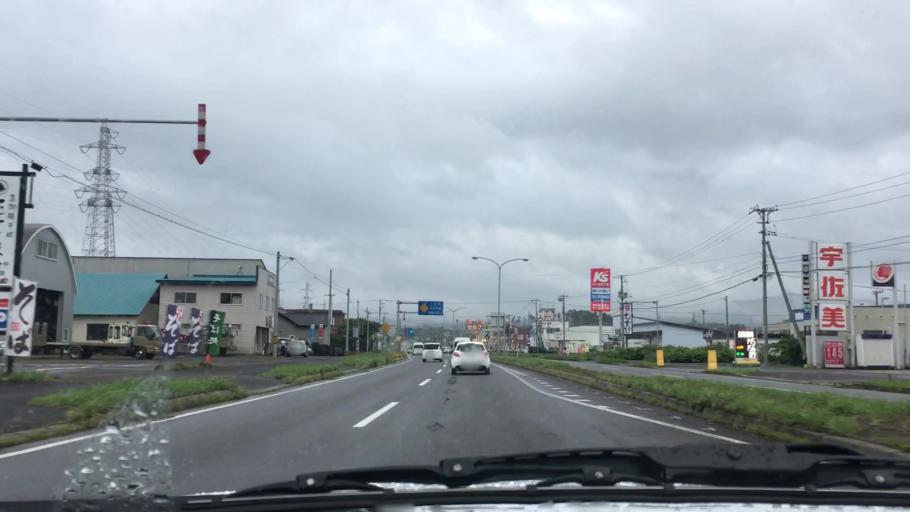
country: JP
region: Hokkaido
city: Nanae
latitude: 42.2504
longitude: 140.2857
